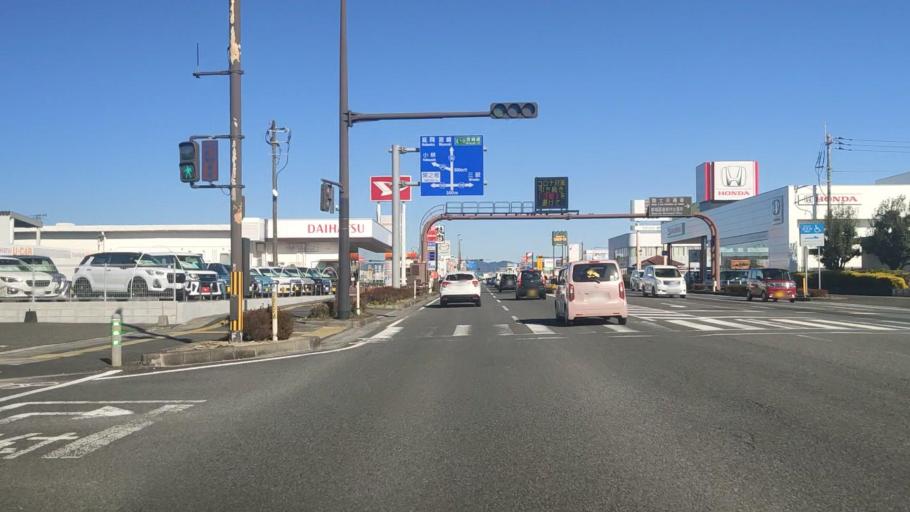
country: JP
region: Miyazaki
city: Miyakonojo
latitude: 31.7600
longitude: 131.0860
